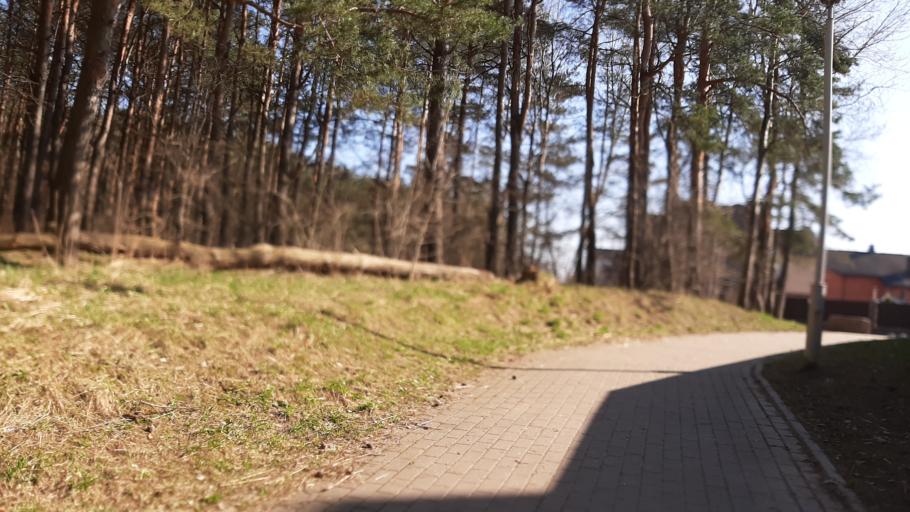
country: BY
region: Minsk
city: Bal'shavik
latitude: 53.9577
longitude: 27.5902
